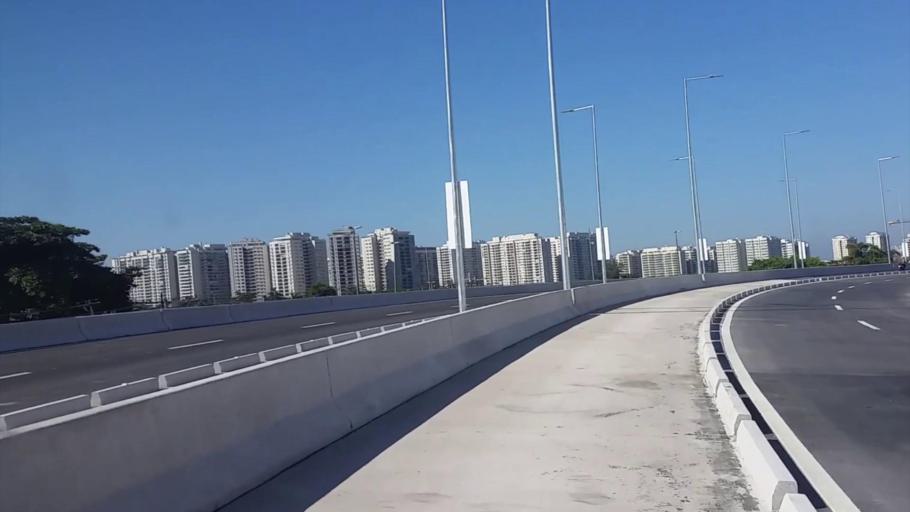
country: BR
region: Rio de Janeiro
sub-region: Nilopolis
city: Nilopolis
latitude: -22.9512
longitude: -43.3898
